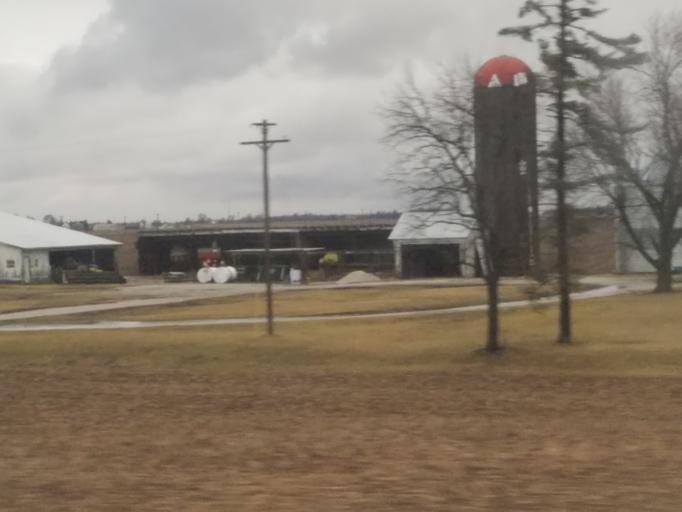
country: US
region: Illinois
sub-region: Warren County
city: Monmouth
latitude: 40.8937
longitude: -90.5688
